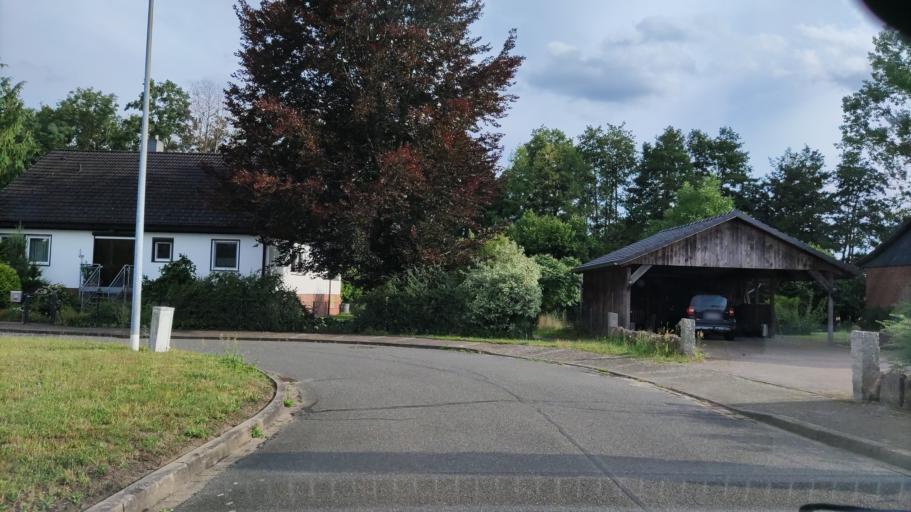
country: DE
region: Lower Saxony
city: Jameln
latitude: 53.0422
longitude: 11.0709
